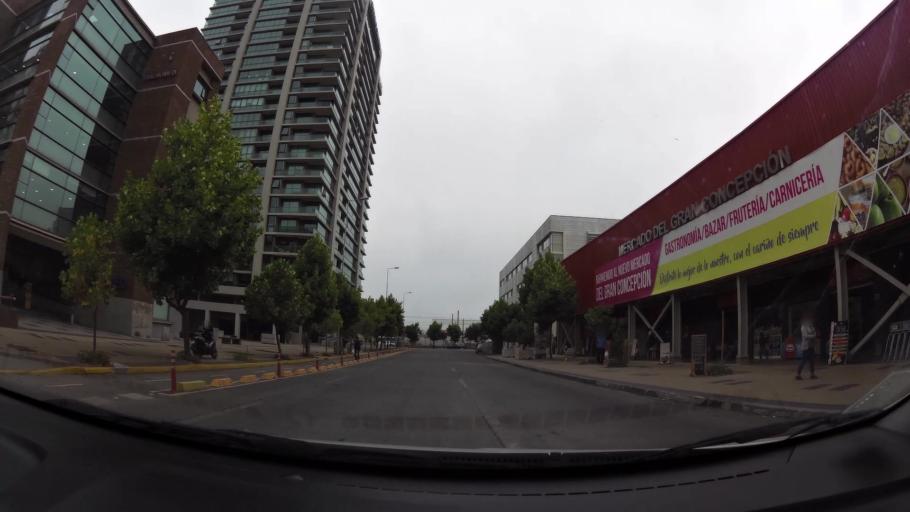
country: CL
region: Biobio
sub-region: Provincia de Concepcion
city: Concepcion
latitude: -36.8312
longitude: -73.0586
